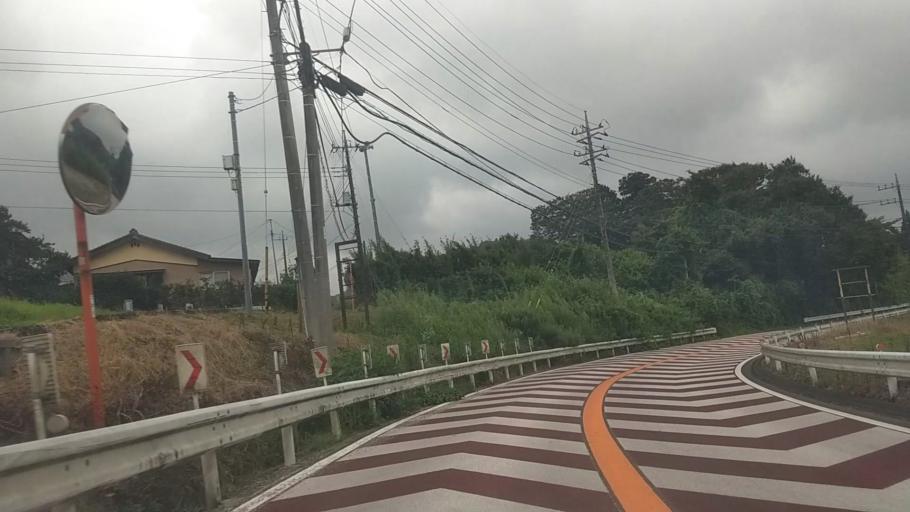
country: JP
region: Chiba
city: Kawaguchi
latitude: 35.2084
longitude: 140.0702
